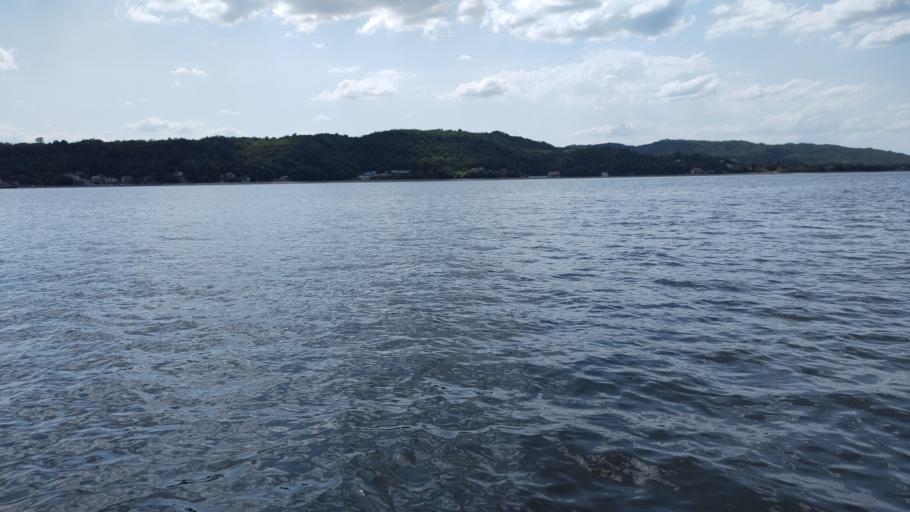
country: RS
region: Central Serbia
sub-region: Branicevski Okrug
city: Golubac
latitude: 44.6612
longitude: 21.6304
